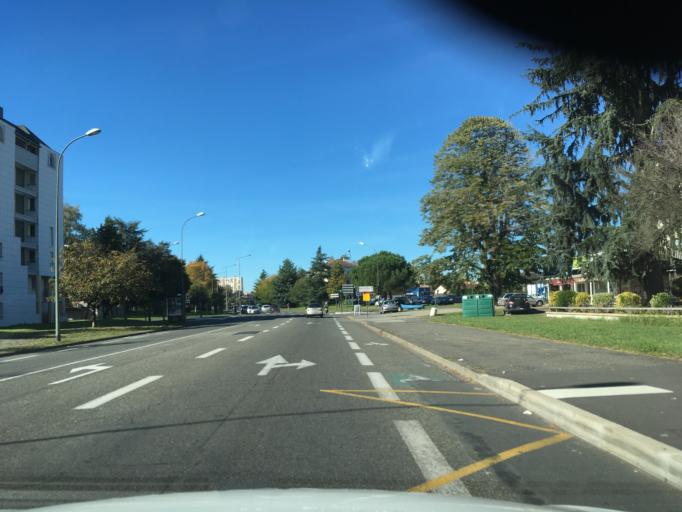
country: FR
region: Aquitaine
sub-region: Departement des Pyrenees-Atlantiques
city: Pau
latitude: 43.3113
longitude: -0.3553
